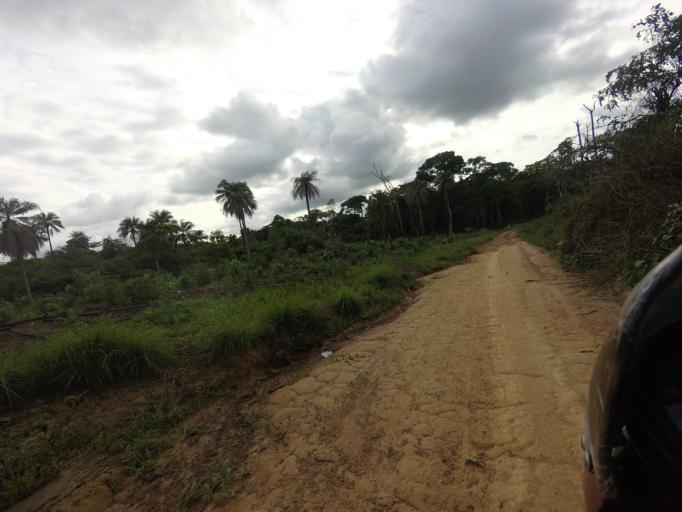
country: SL
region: Eastern Province
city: Jojoima
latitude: 7.7924
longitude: -10.8120
